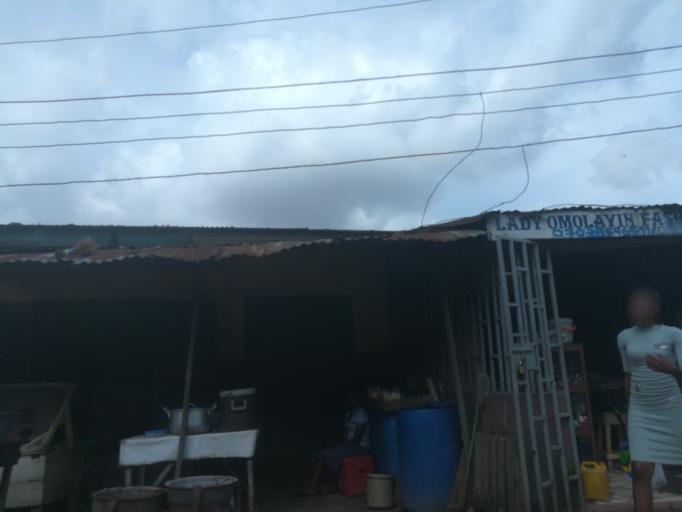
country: NG
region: Lagos
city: Somolu
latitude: 6.5299
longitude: 3.3835
